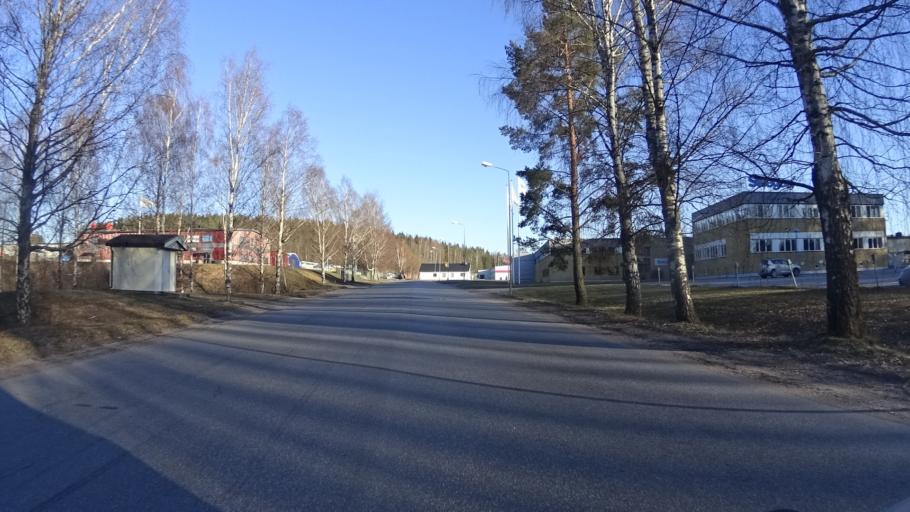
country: SE
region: Vaermland
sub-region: Arvika Kommun
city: Arvika
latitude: 59.6609
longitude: 12.6261
